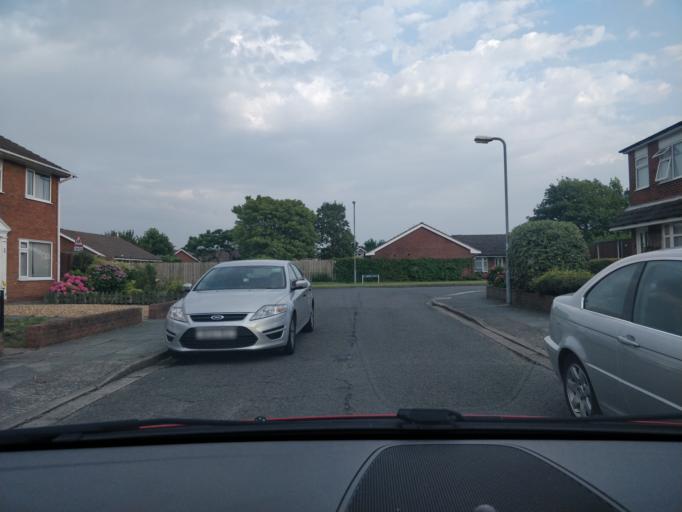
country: GB
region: England
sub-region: Sefton
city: Southport
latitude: 53.6730
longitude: -2.9714
